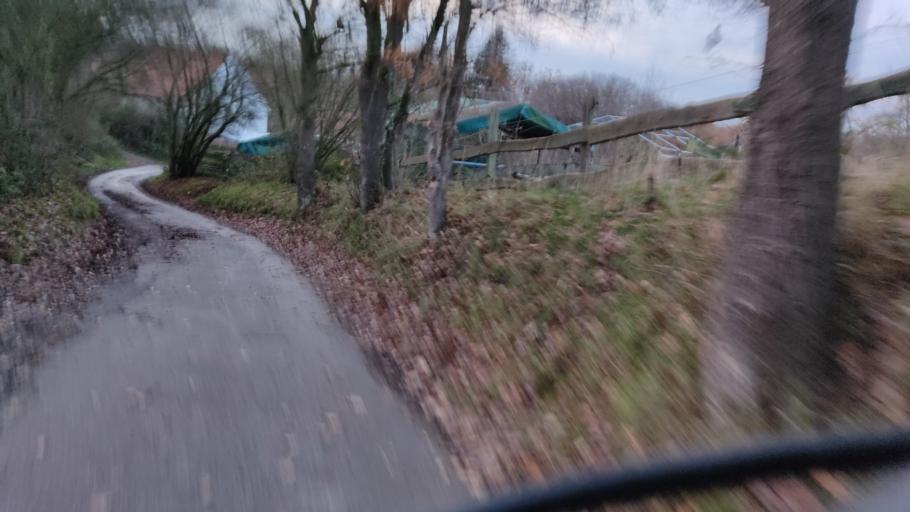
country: DE
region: North Rhine-Westphalia
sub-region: Regierungsbezirk Dusseldorf
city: Velbert
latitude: 51.3800
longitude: 7.1024
